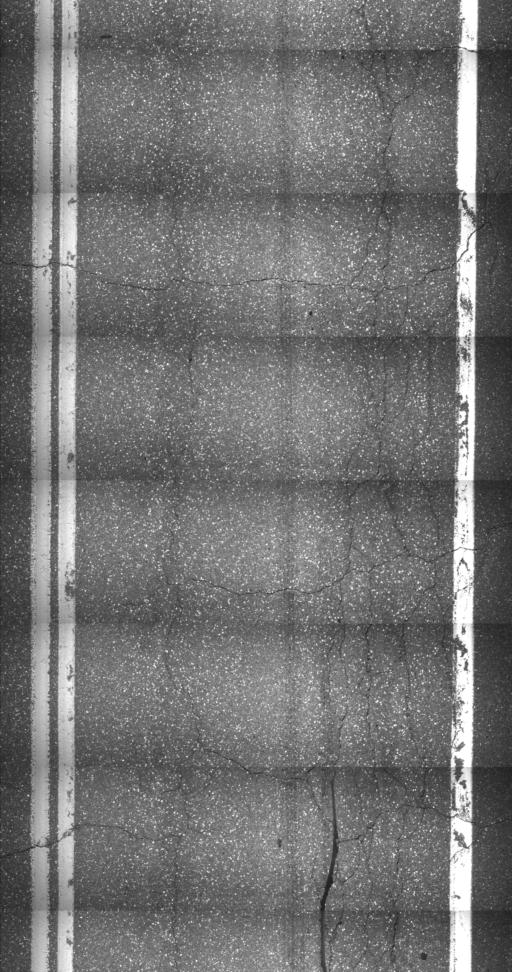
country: US
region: Vermont
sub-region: Windsor County
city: Windsor
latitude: 43.4731
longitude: -72.5361
